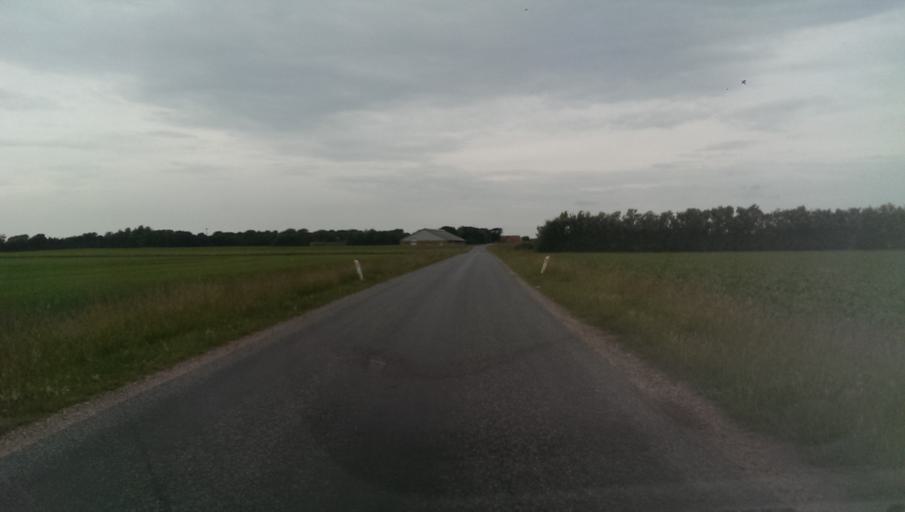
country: DK
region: South Denmark
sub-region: Esbjerg Kommune
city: Bramming
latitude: 55.4396
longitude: 8.6491
